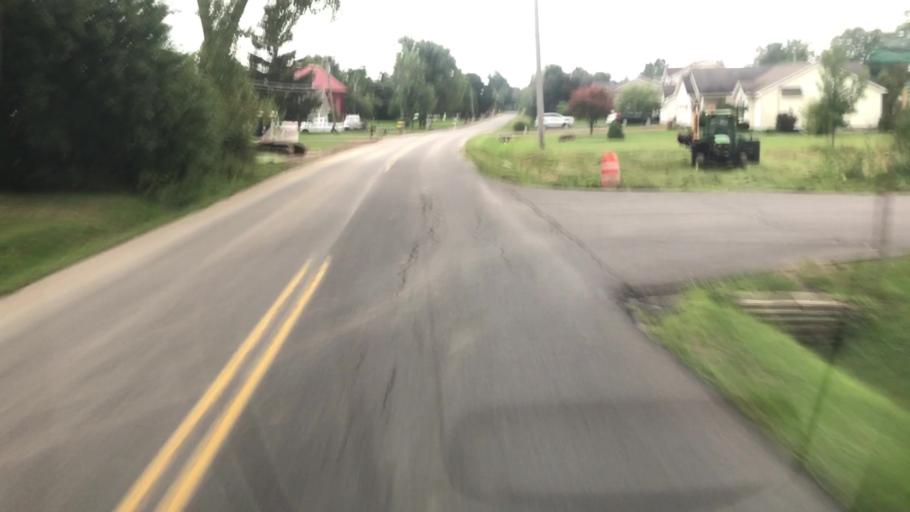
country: US
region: New York
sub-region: Cayuga County
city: Melrose Park
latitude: 42.9127
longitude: -76.5295
